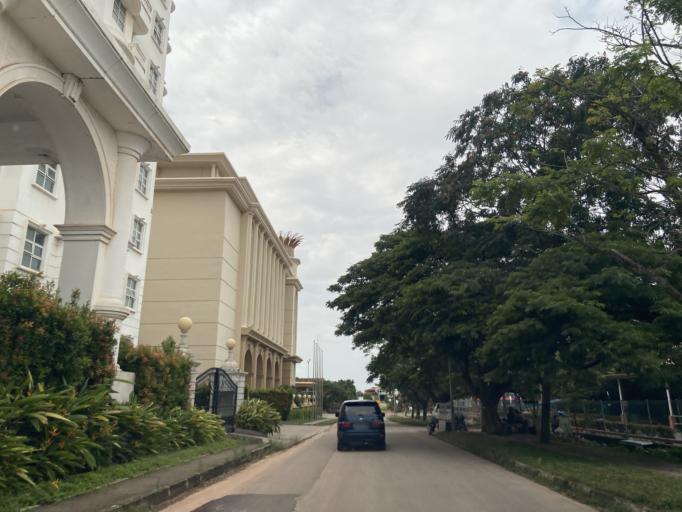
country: SG
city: Singapore
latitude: 1.1311
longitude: 104.0481
